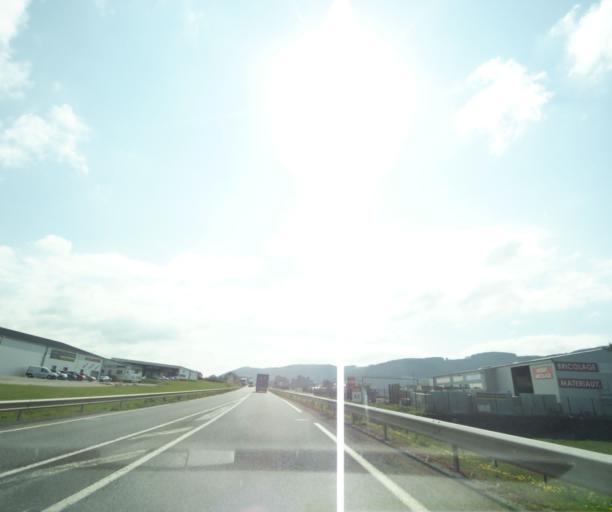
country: FR
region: Midi-Pyrenees
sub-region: Departement de l'Aveyron
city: Laissac
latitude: 44.3745
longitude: 2.8347
